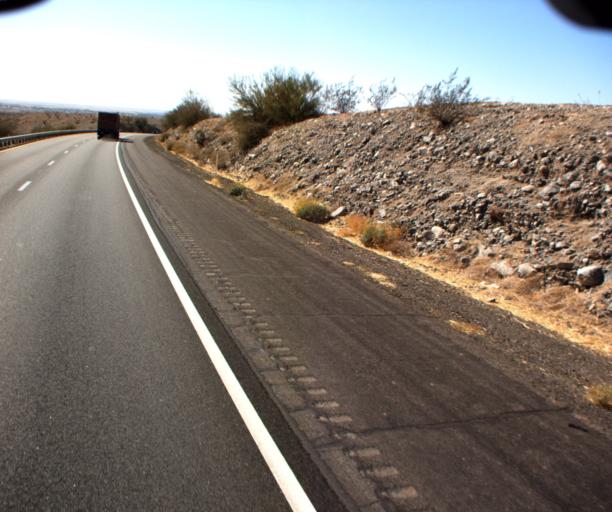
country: US
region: Arizona
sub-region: Yuma County
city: Fortuna Foothills
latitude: 32.6592
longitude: -114.3390
